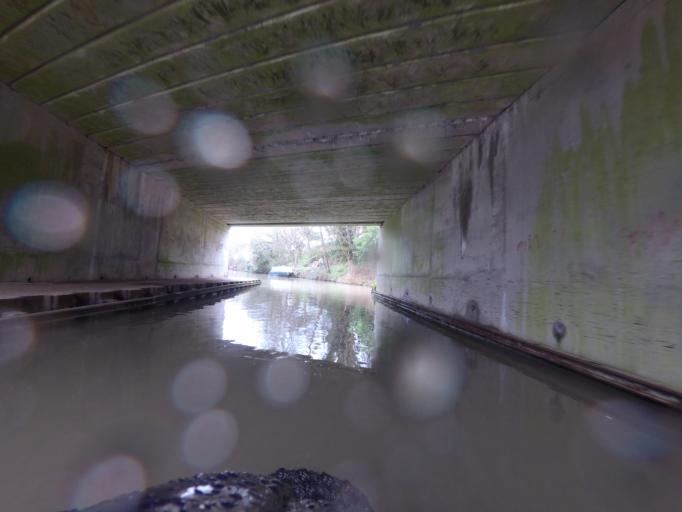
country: GB
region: England
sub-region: Milton Keynes
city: Stony Stratford
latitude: 52.0648
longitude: -0.8258
